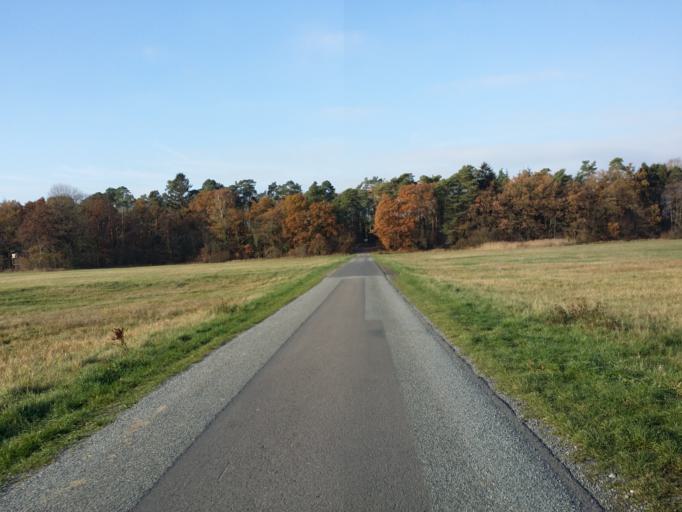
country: DE
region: Lower Saxony
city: Ahausen
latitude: 53.0980
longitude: 9.3553
